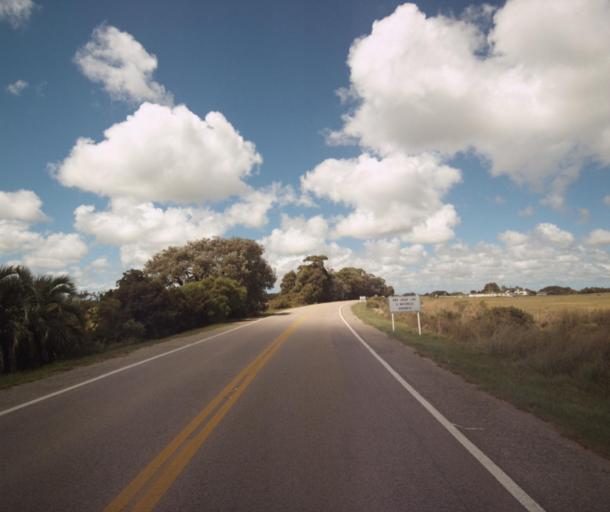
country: BR
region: Rio Grande do Sul
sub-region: Arroio Grande
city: Arroio Grande
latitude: -32.5342
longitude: -52.5385
